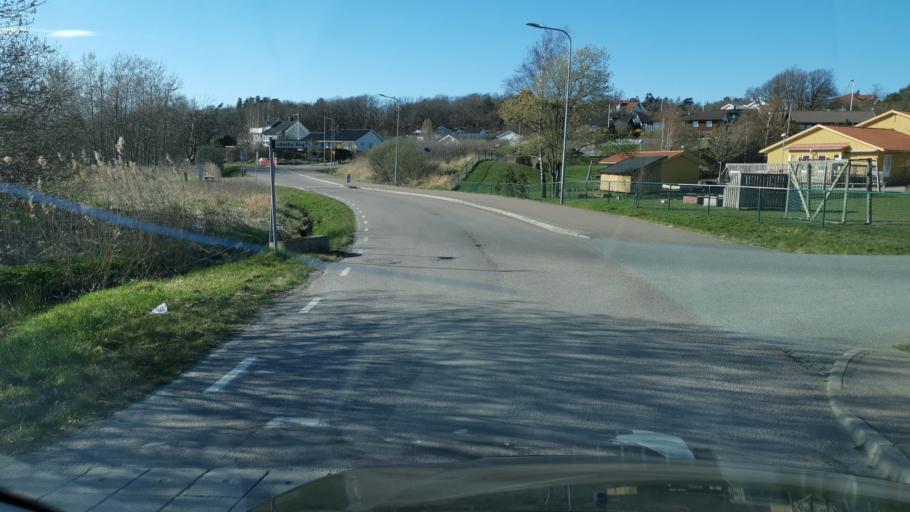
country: SE
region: Vaestra Goetaland
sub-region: Goteborg
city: Torslanda
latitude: 57.7424
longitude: 11.8269
